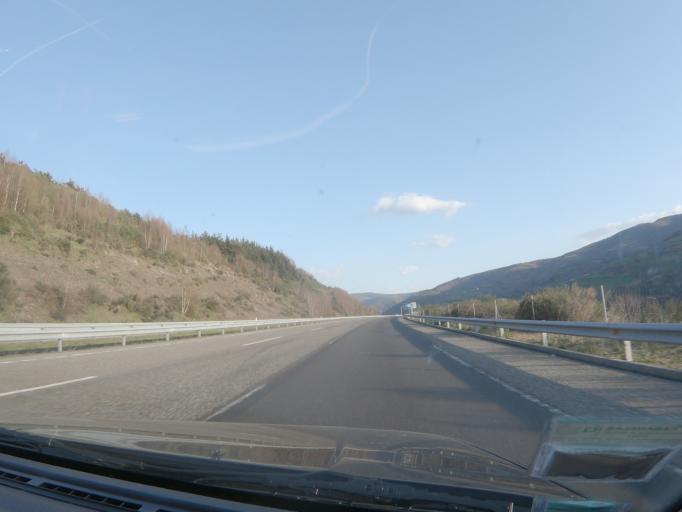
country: ES
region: Galicia
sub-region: Provincia de Lugo
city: San Roman
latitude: 42.7700
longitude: -7.0895
